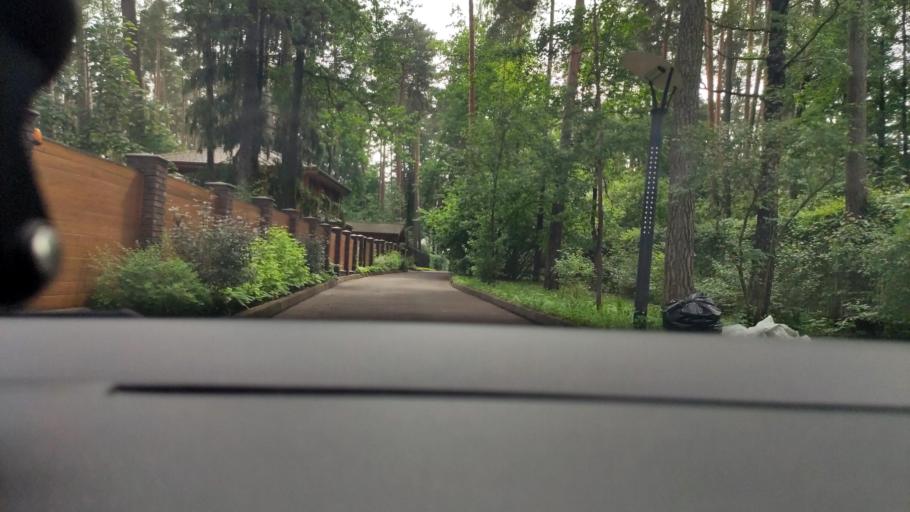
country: RU
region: Moskovskaya
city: Nikolina Gora
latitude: 55.7343
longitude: 37.0754
